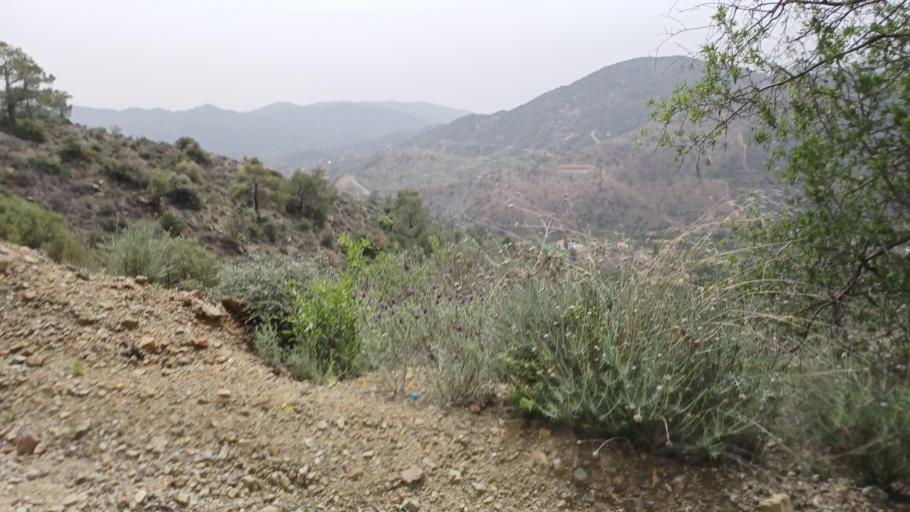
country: CY
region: Limassol
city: Parekklisha
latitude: 34.8530
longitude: 33.1092
